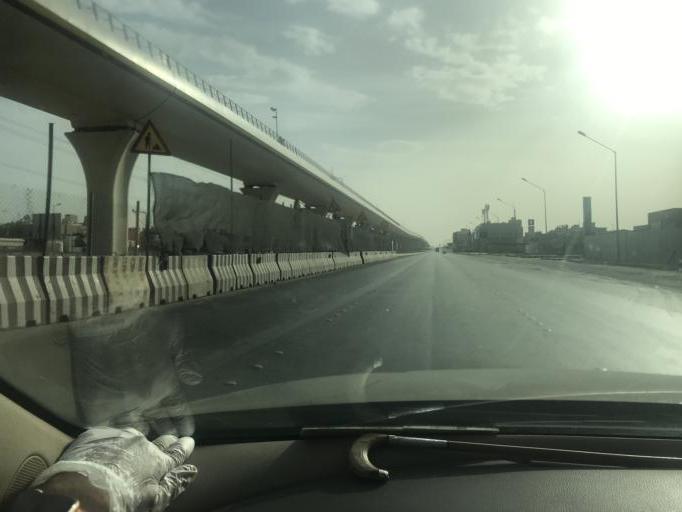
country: SA
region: Ar Riyad
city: Riyadh
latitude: 24.8009
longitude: 46.6942
